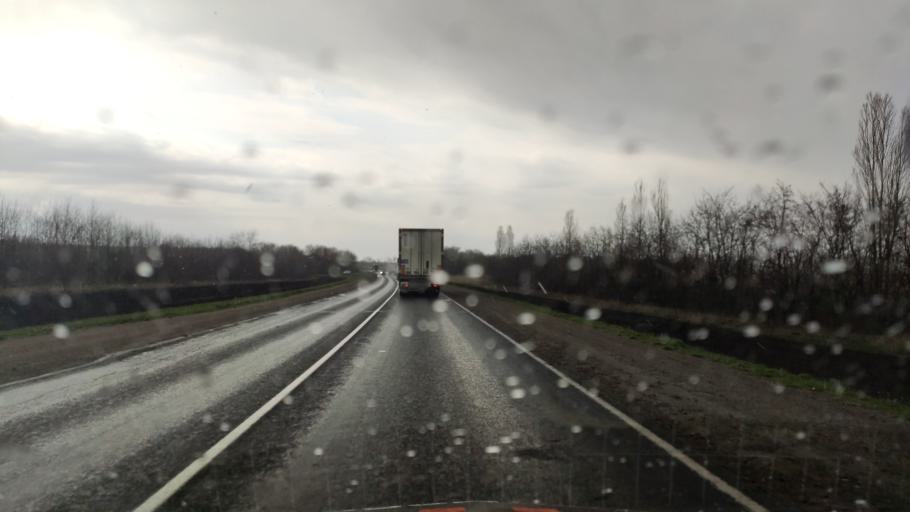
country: RU
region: Voronezj
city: Nizhnedevitsk
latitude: 51.5741
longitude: 38.3274
